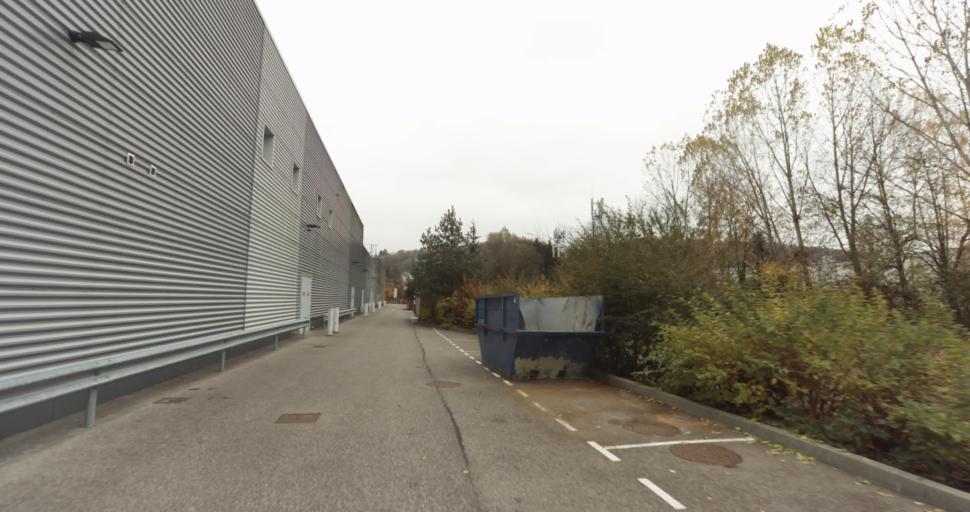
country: FR
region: Rhone-Alpes
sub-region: Departement de la Haute-Savoie
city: Epagny
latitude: 45.9349
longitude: 6.0806
